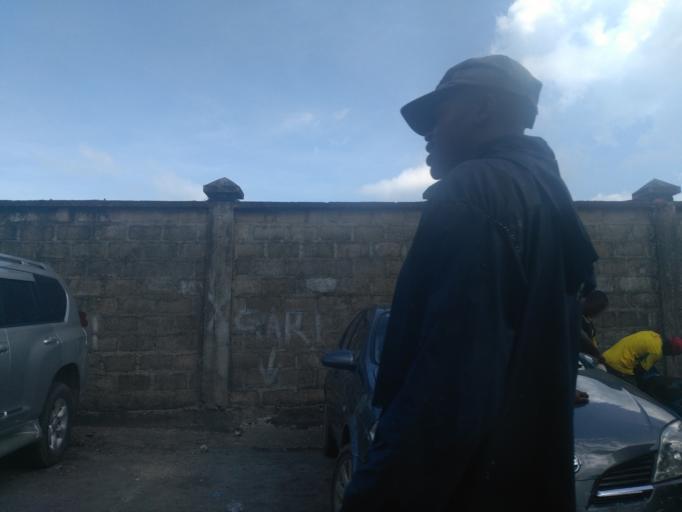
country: TZ
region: Zanzibar Urban/West
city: Zanzibar
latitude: -6.1558
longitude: 39.1951
